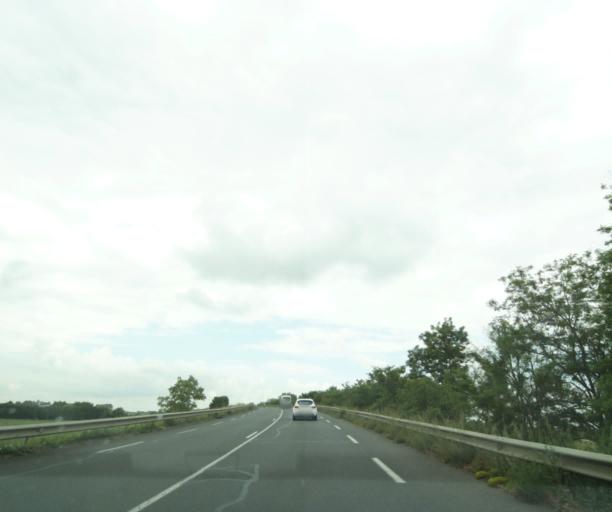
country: FR
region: Poitou-Charentes
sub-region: Departement des Deux-Sevres
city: Louzy
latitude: 47.0086
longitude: -0.1952
